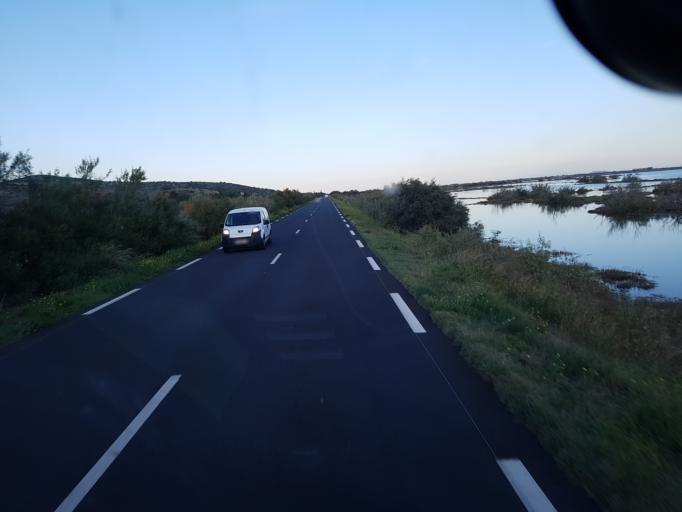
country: FR
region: Languedoc-Roussillon
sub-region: Departement de l'Aude
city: Sigean
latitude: 42.9752
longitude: 3.0054
